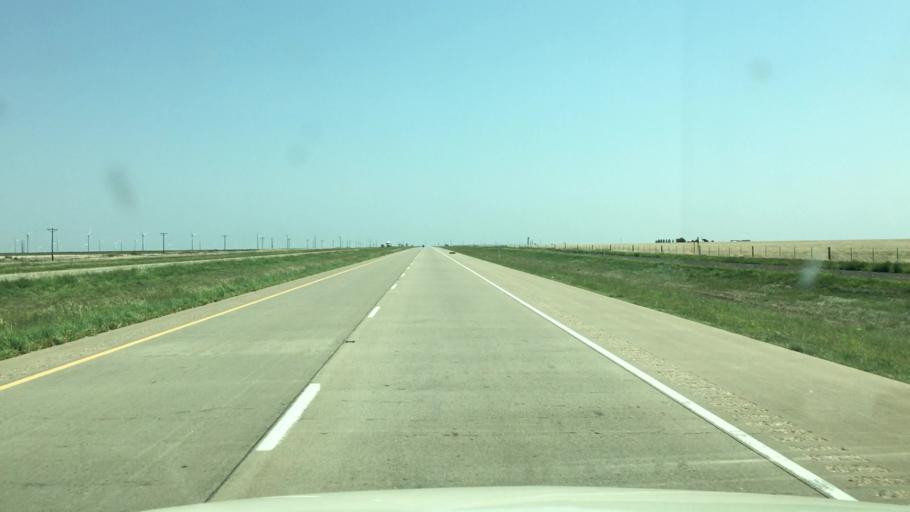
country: US
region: Texas
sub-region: Oldham County
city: Vega
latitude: 35.2728
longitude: -102.6098
